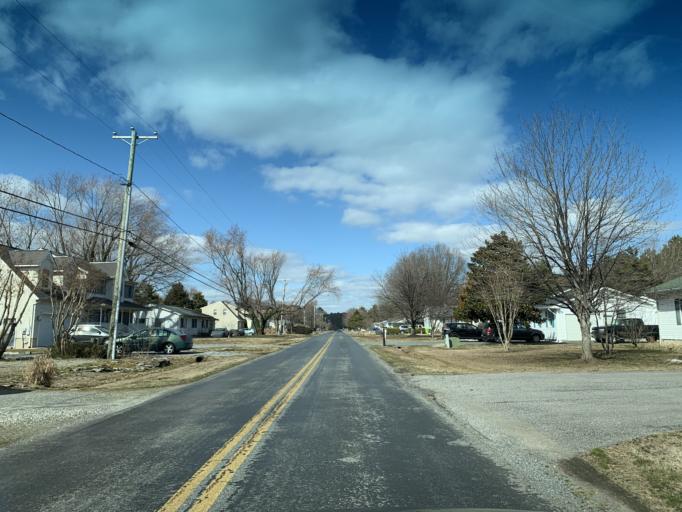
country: US
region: Maryland
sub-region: Queen Anne's County
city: Chester
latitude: 38.9357
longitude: -76.2658
